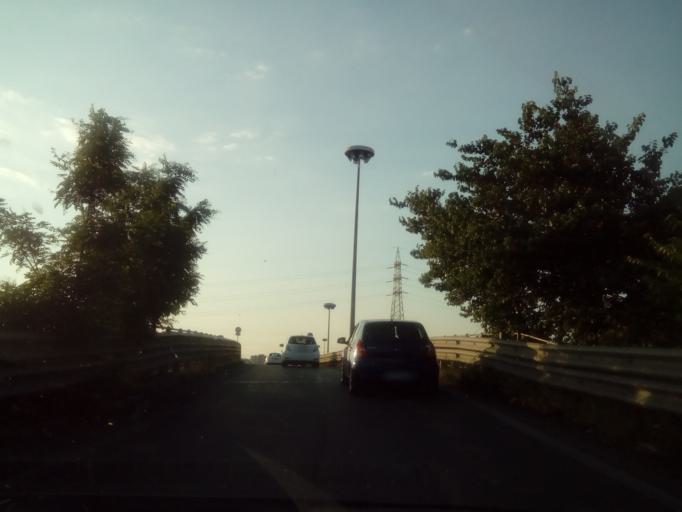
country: IT
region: Latium
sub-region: Citta metropolitana di Roma Capitale
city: Rome
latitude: 41.9024
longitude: 12.5750
